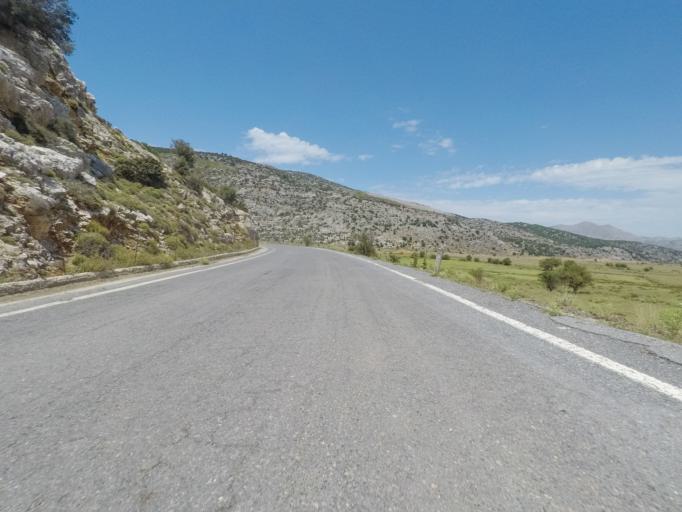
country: GR
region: Crete
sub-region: Nomos Irakleiou
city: Mokhos
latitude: 35.1896
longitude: 25.4320
